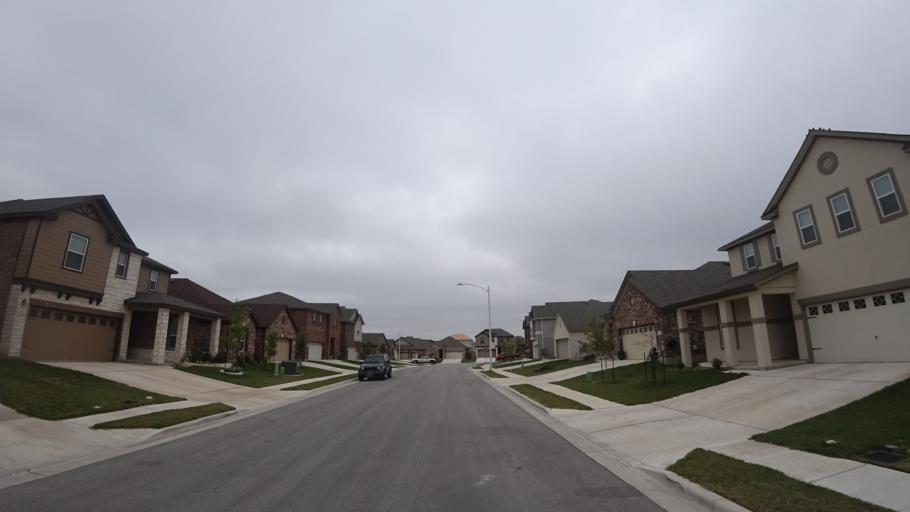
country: US
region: Texas
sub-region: Travis County
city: Pflugerville
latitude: 30.3934
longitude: -97.6492
